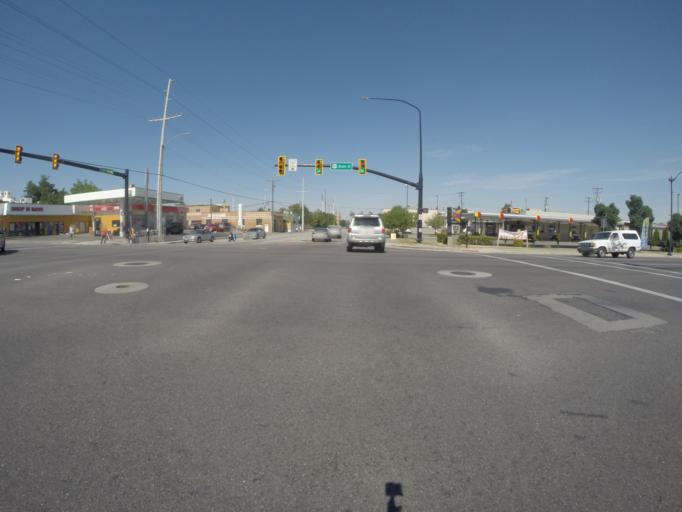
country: US
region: Utah
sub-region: Salt Lake County
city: Salt Lake City
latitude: 40.7418
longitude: -111.8881
